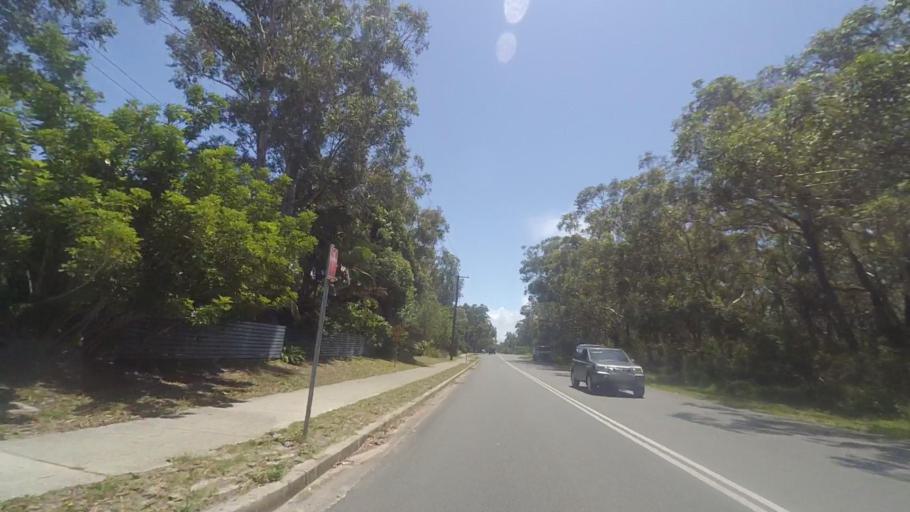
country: AU
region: New South Wales
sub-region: Great Lakes
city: Hawks Nest
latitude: -32.6696
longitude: 152.1779
